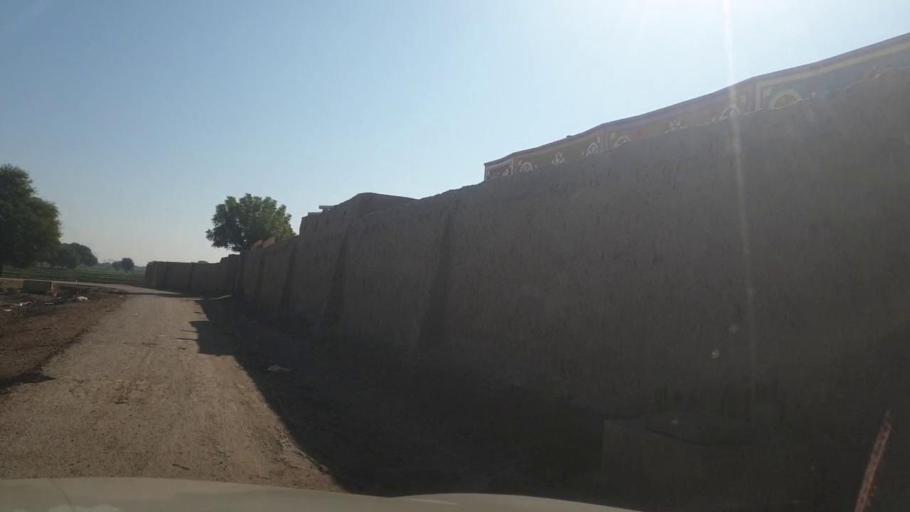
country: PK
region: Sindh
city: Bhan
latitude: 26.5446
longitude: 67.6623
